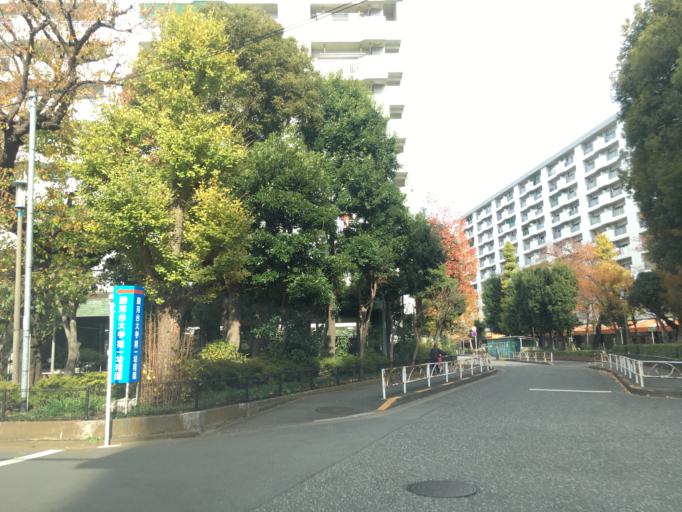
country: JP
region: Tokyo
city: Chofugaoka
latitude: 35.6481
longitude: 139.5609
